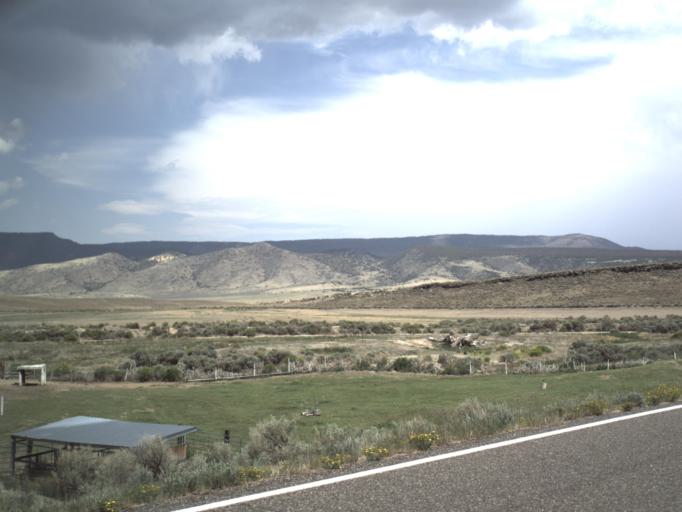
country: US
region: Utah
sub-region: Piute County
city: Junction
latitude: 38.1603
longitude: -112.0084
